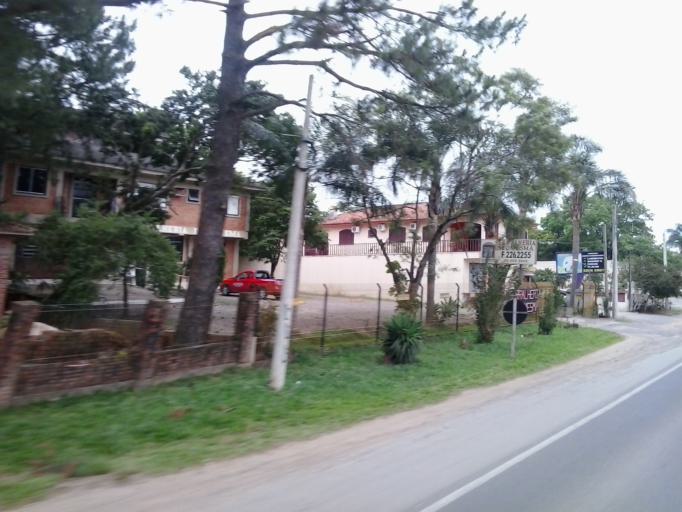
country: BR
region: Rio Grande do Sul
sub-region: Santa Maria
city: Santa Maria
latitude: -29.6941
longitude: -53.7525
